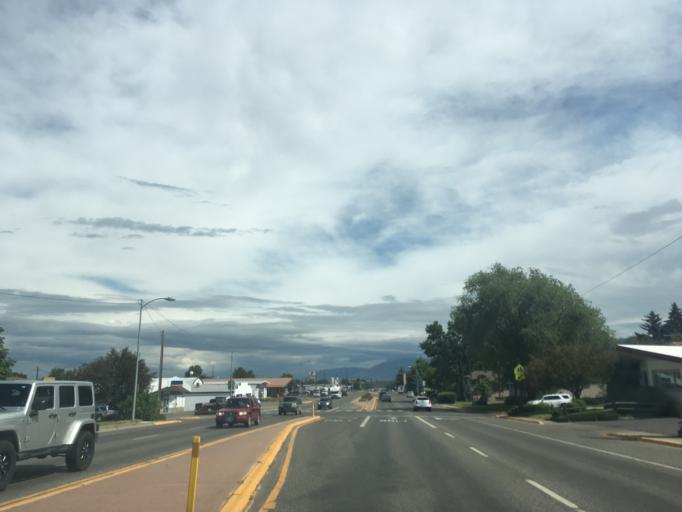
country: US
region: Montana
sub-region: Gallatin County
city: Bozeman
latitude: 45.6823
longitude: -111.0462
